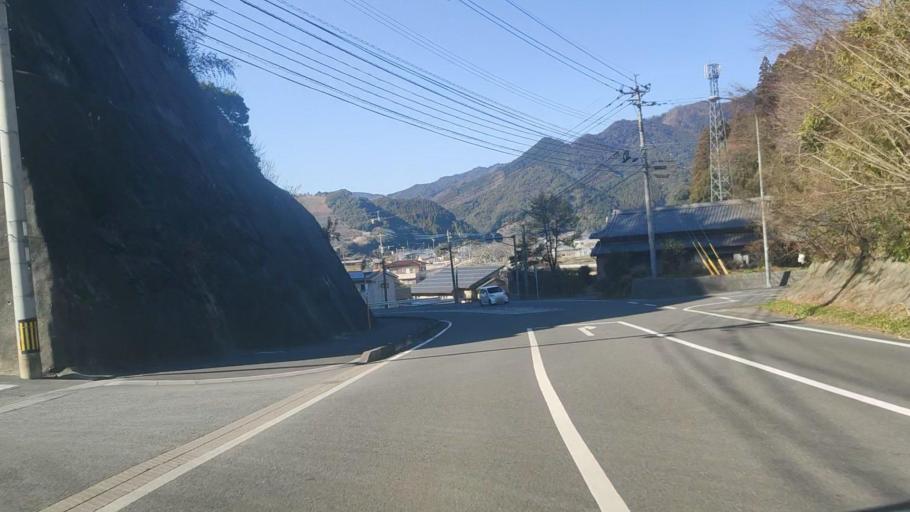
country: JP
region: Oita
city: Saiki
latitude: 32.9763
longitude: 131.8535
